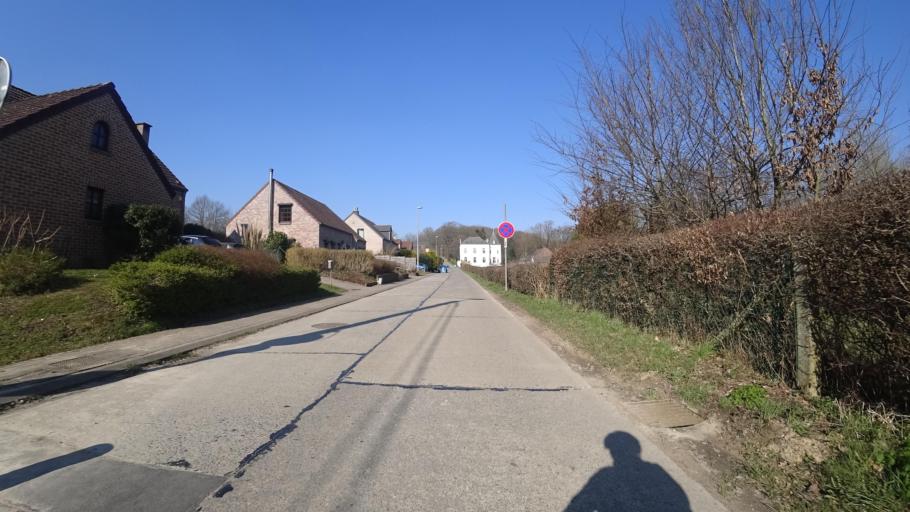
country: BE
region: Wallonia
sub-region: Province du Brabant Wallon
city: Mont-Saint-Guibert
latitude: 50.6267
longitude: 4.6125
